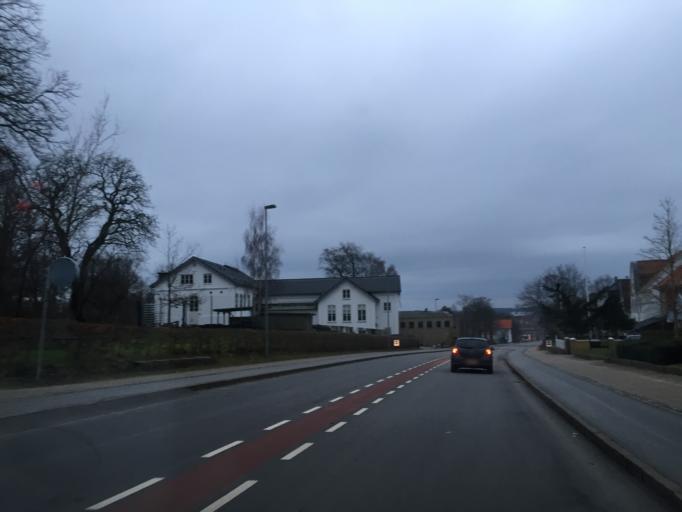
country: DK
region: South Denmark
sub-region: Haderslev Kommune
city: Haderslev
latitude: 55.2587
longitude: 9.4930
